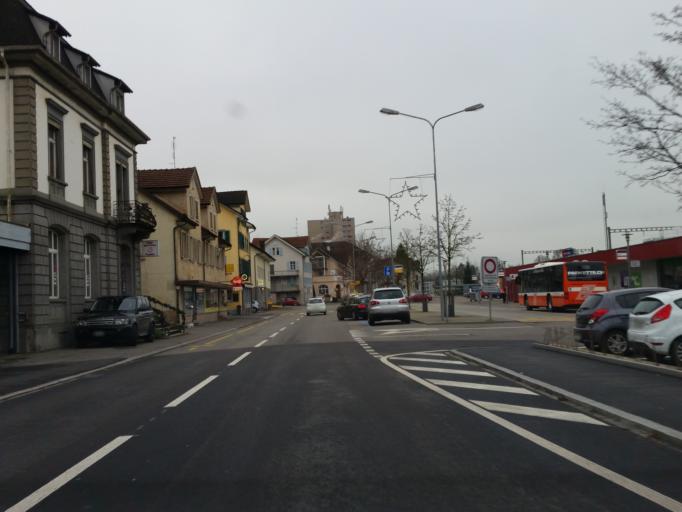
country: CH
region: Thurgau
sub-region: Arbon District
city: Amriswil
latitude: 47.5501
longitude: 9.3029
